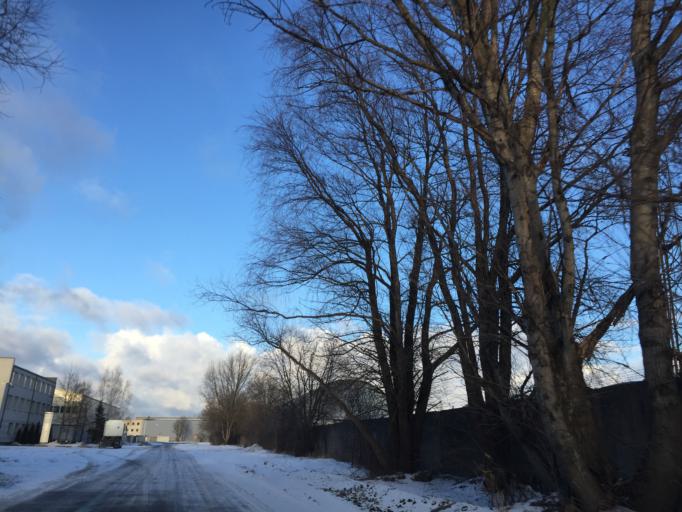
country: LV
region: Riga
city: Riga
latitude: 56.9869
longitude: 24.1115
